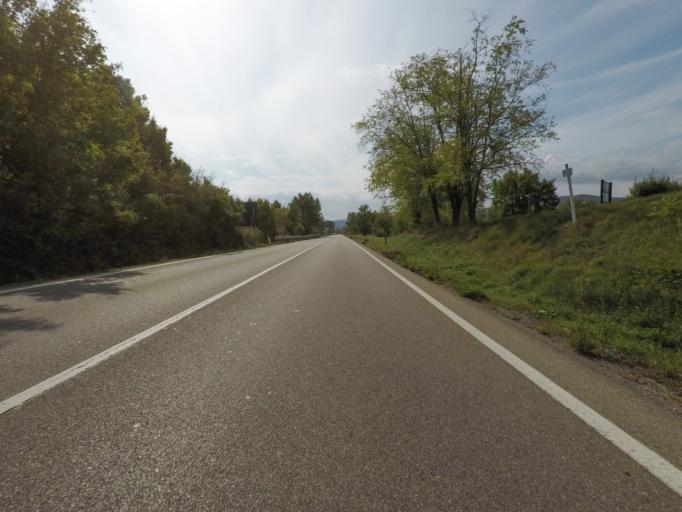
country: IT
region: Tuscany
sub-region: Provincia di Siena
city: Rosia
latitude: 43.2074
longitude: 11.2788
